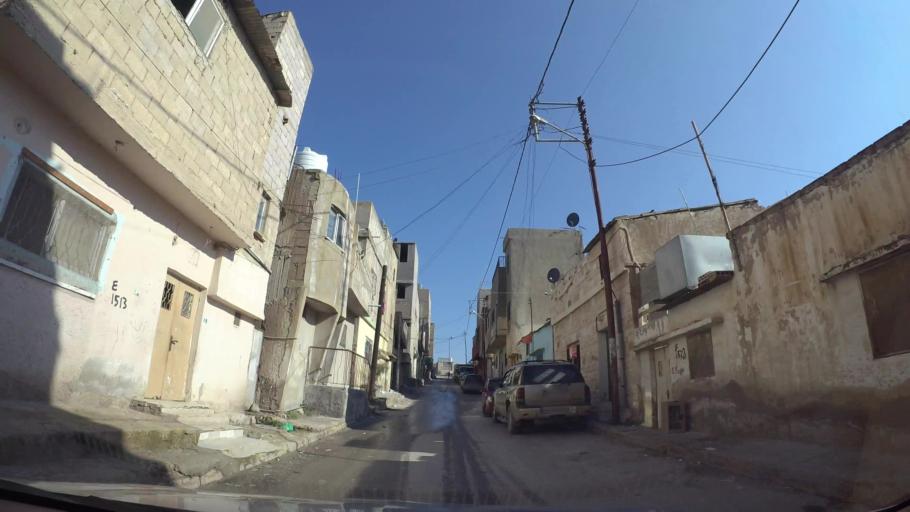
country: JO
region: Amman
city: Al Jubayhah
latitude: 32.0673
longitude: 35.8445
